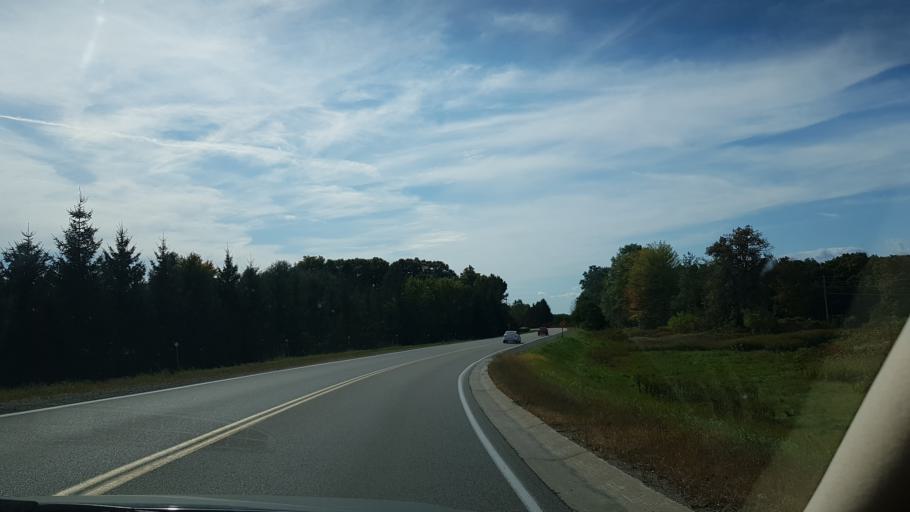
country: CA
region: Ontario
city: Delaware
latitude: 42.9709
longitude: -81.3943
